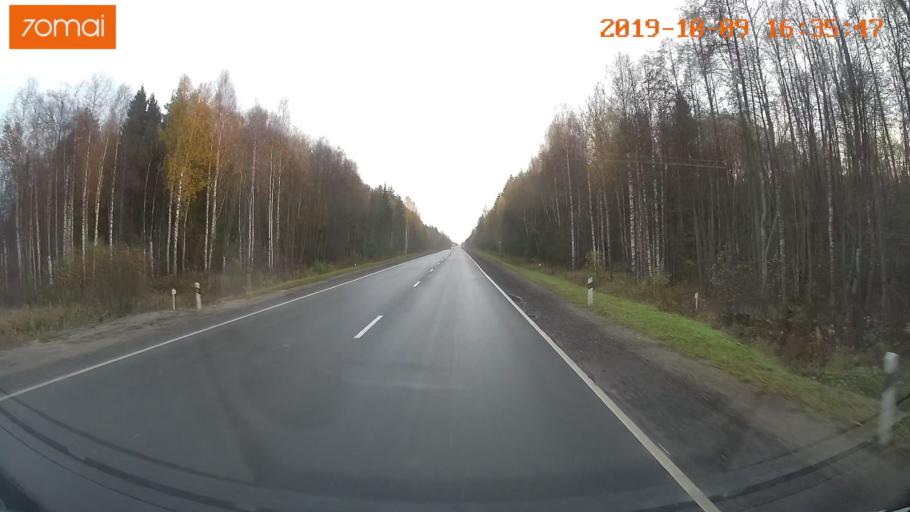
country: RU
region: Kostroma
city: Volgorechensk
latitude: 57.5508
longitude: 41.0049
